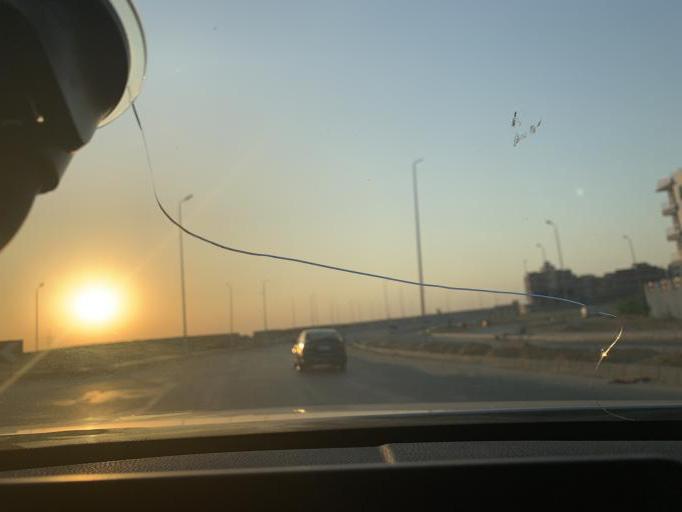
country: EG
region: Muhafazat al Qahirah
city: Halwan
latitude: 29.9762
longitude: 31.4709
